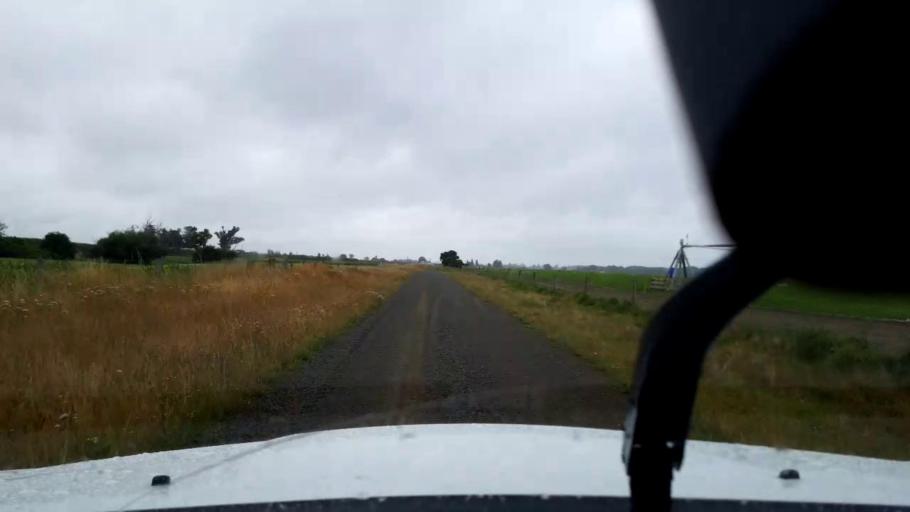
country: NZ
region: Canterbury
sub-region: Timaru District
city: Pleasant Point
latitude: -44.2539
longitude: 171.1917
